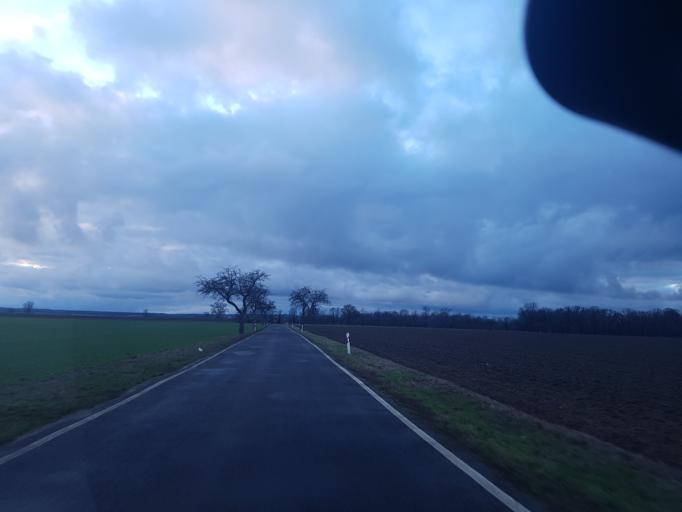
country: DE
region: Brandenburg
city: Muhlberg
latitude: 51.4636
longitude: 13.2124
